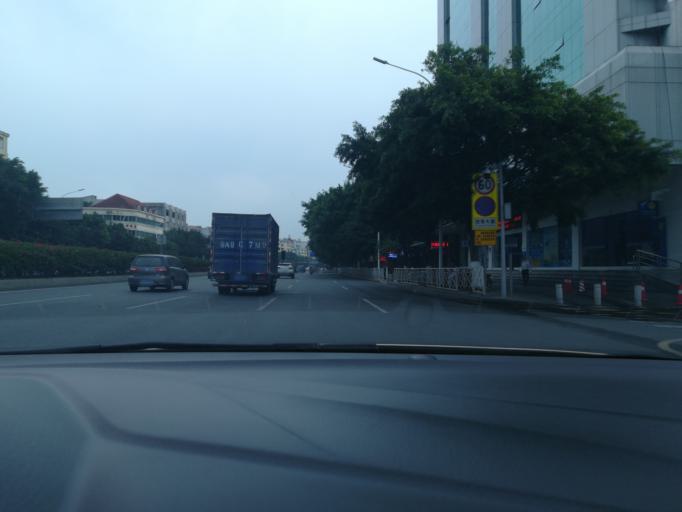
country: CN
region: Guangdong
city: Nansha
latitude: 22.8031
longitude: 113.5414
